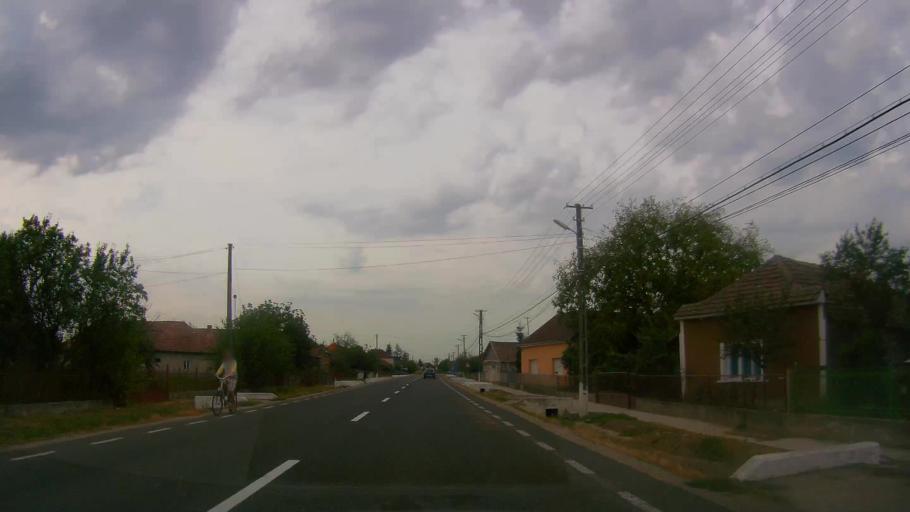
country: RO
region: Satu Mare
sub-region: Comuna Acas
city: Acas
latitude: 47.5315
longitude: 22.7828
